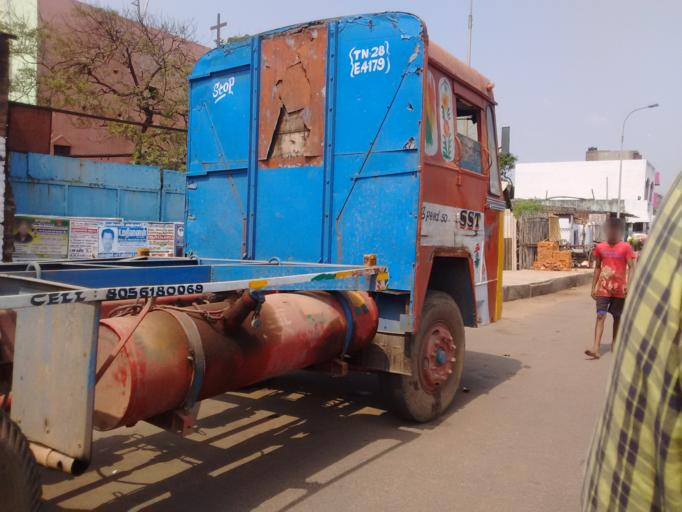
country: IN
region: Tamil Nadu
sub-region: Thiruvallur
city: Tiruvottiyur
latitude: 13.1605
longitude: 80.3059
